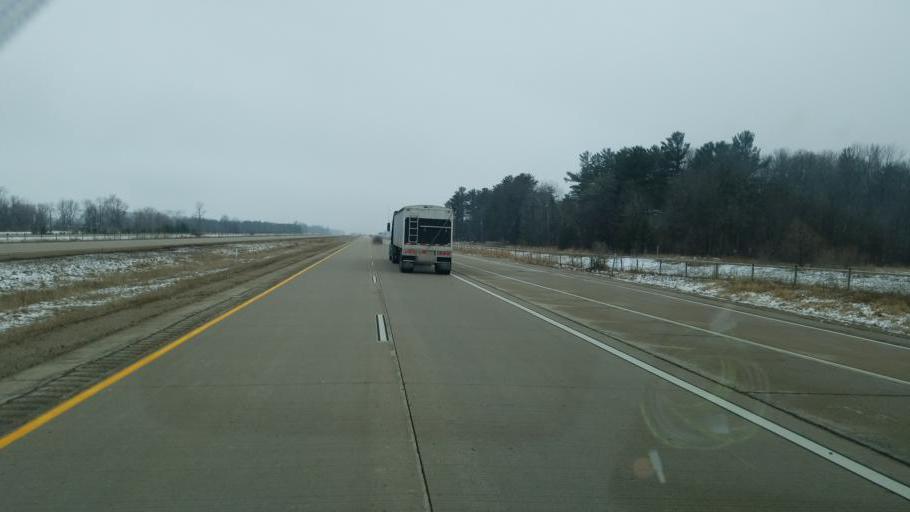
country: US
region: Wisconsin
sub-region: Winnebago County
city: Winneconne
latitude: 44.2343
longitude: -88.7438
